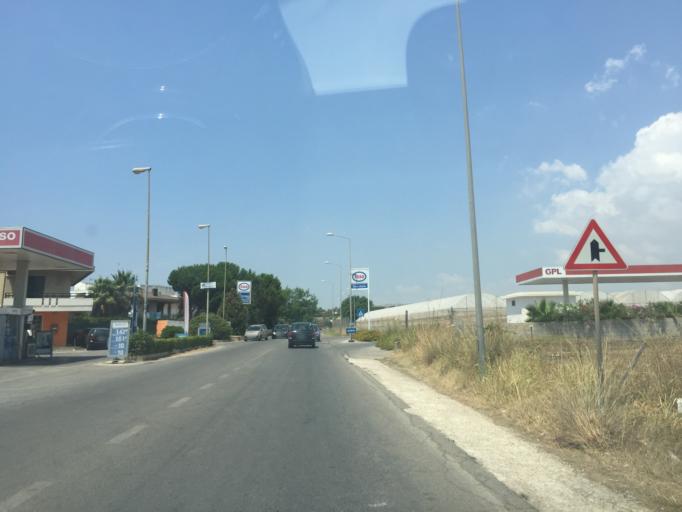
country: IT
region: Sicily
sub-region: Ragusa
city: Donnalucata
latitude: 36.7722
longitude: 14.6099
